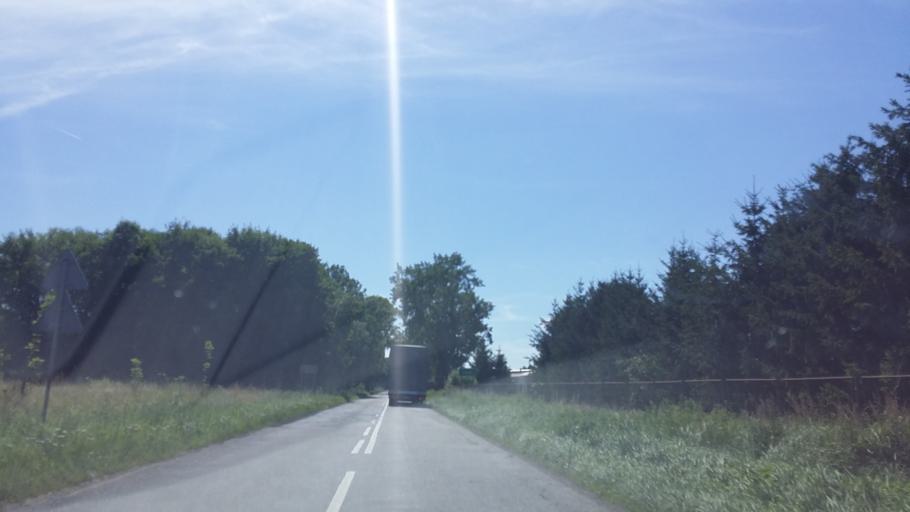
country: PL
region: West Pomeranian Voivodeship
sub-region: Powiat lobeski
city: Lobez
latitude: 53.6468
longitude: 15.6380
